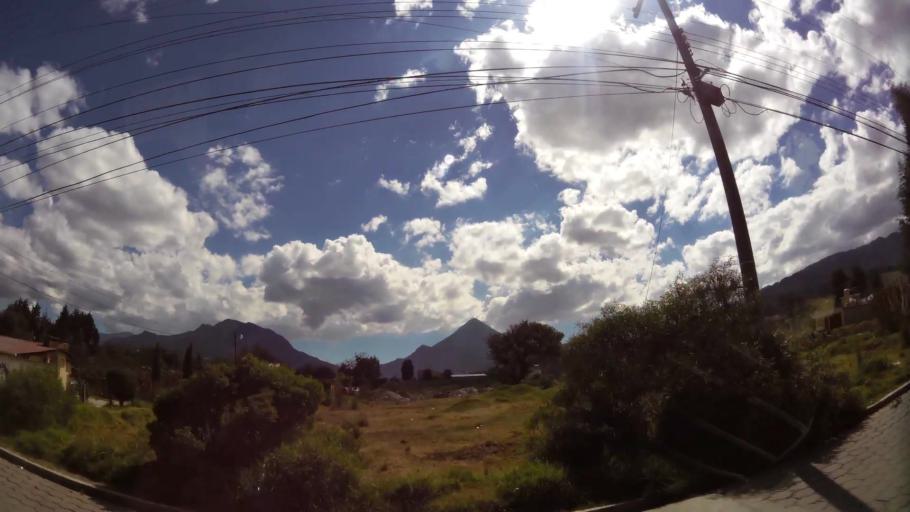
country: GT
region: Quetzaltenango
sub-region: Municipio de La Esperanza
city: La Esperanza
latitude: 14.8473
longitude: -91.5451
